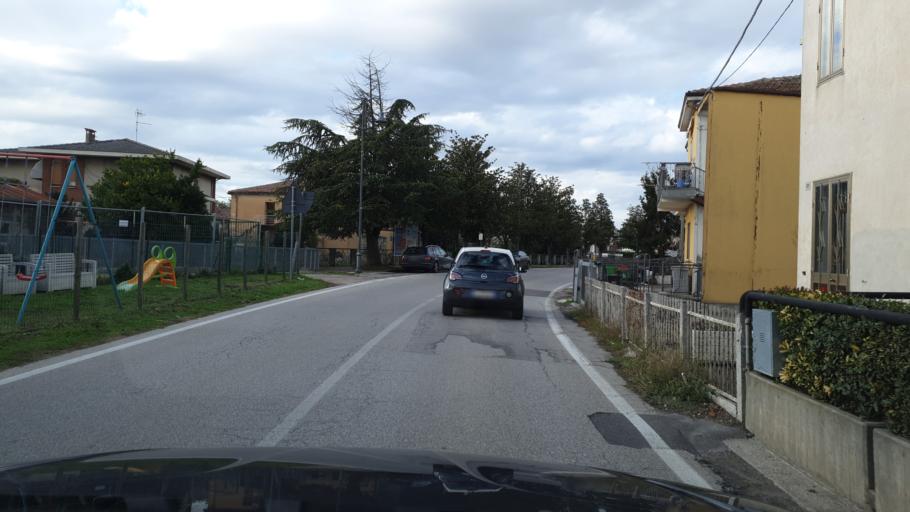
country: IT
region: Veneto
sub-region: Provincia di Rovigo
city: Villanova del Ghebbo Canton
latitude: 45.0531
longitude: 11.6460
